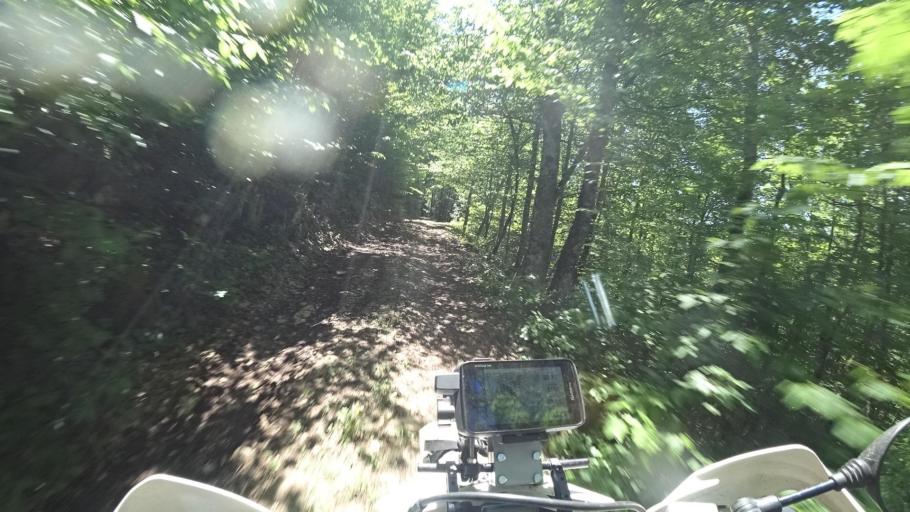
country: BA
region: Republika Srpska
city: Skender Vakuf
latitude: 44.4896
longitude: 17.2392
